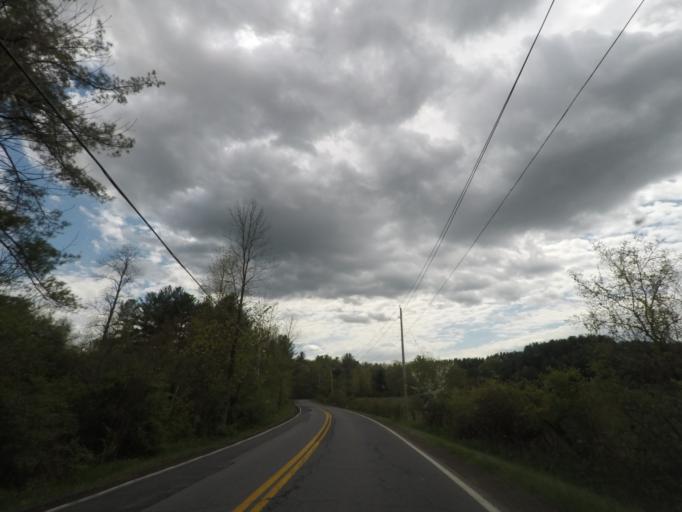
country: US
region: New York
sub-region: Albany County
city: Westmere
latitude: 42.6980
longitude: -73.9135
